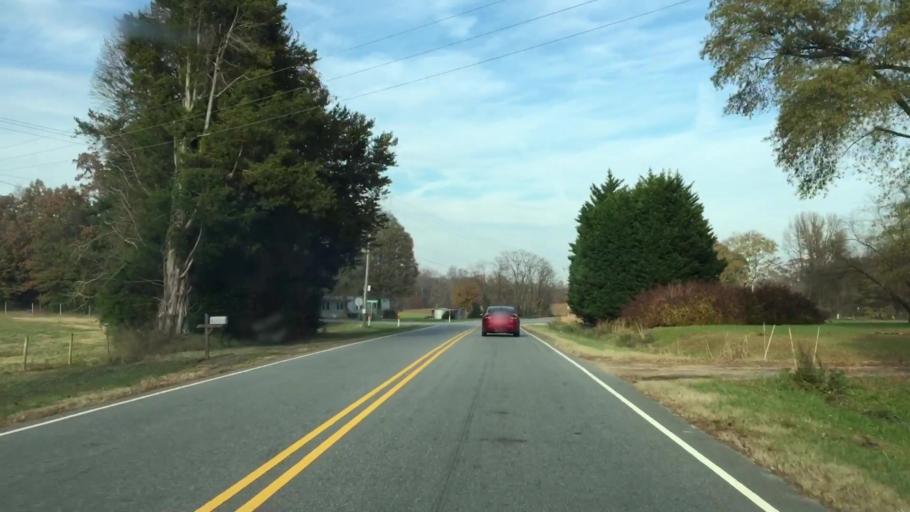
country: US
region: North Carolina
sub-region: Rockingham County
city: Reidsville
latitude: 36.2863
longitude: -79.7512
